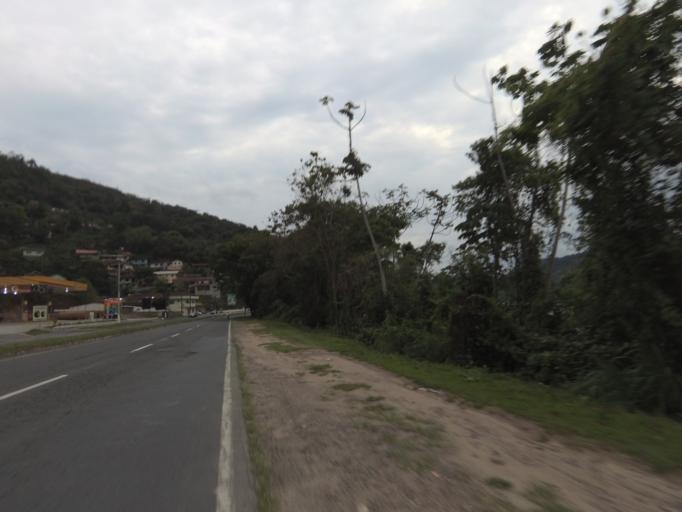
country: BR
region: Santa Catarina
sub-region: Blumenau
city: Blumenau
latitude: -26.8971
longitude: -49.0587
